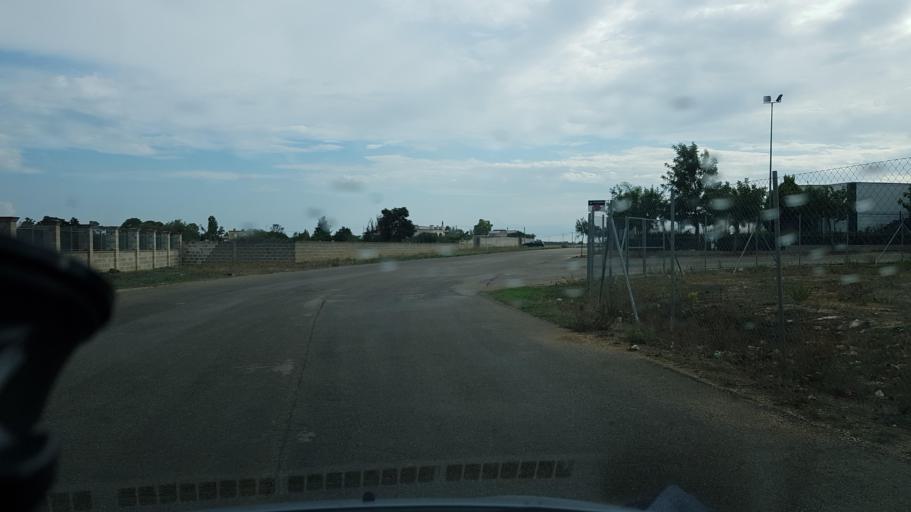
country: IT
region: Apulia
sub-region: Provincia di Brindisi
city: Torre Santa Susanna
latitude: 40.4705
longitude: 17.7243
